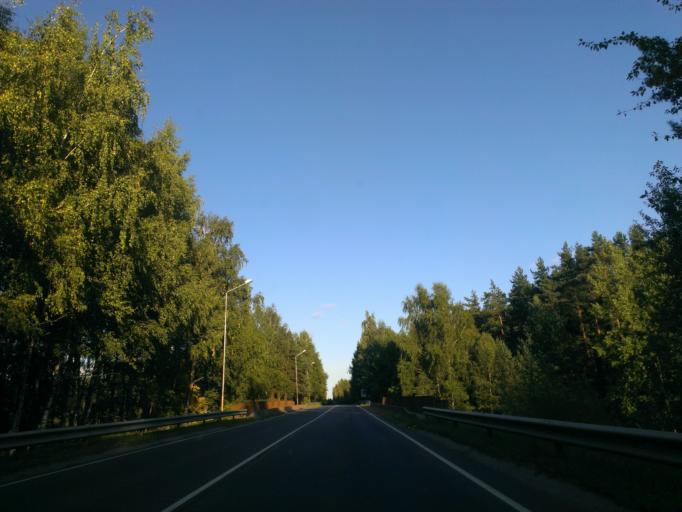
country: LV
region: Riga
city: Bergi
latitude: 57.0023
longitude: 24.2717
